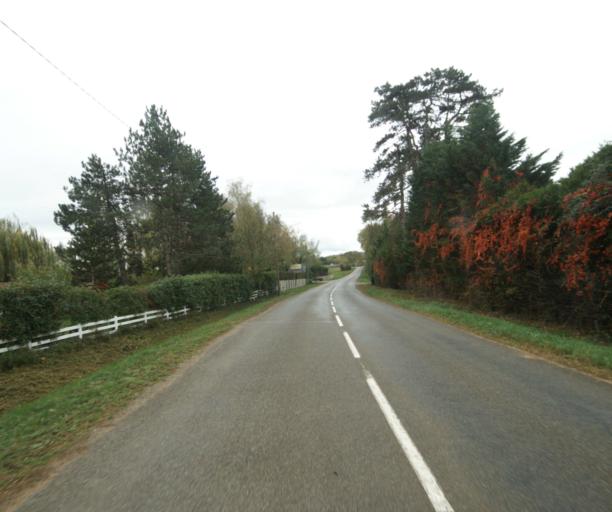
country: FR
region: Rhone-Alpes
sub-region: Departement de l'Ain
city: Pont-de-Vaux
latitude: 46.4643
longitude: 4.8720
